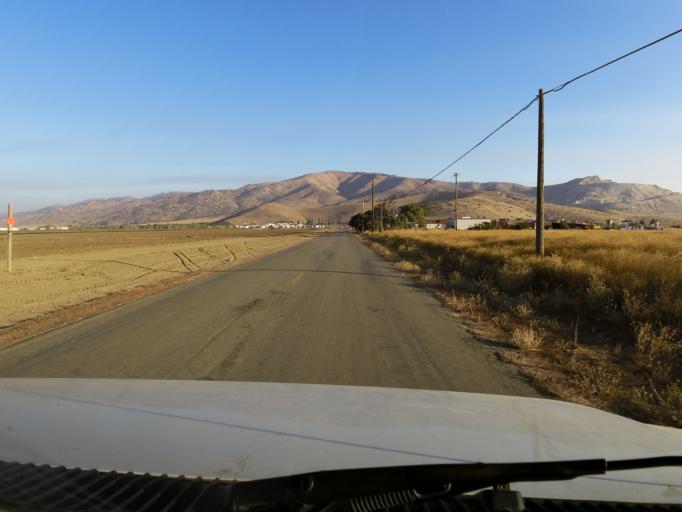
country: US
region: California
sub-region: Kern County
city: Tehachapi
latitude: 35.1199
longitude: -118.4144
